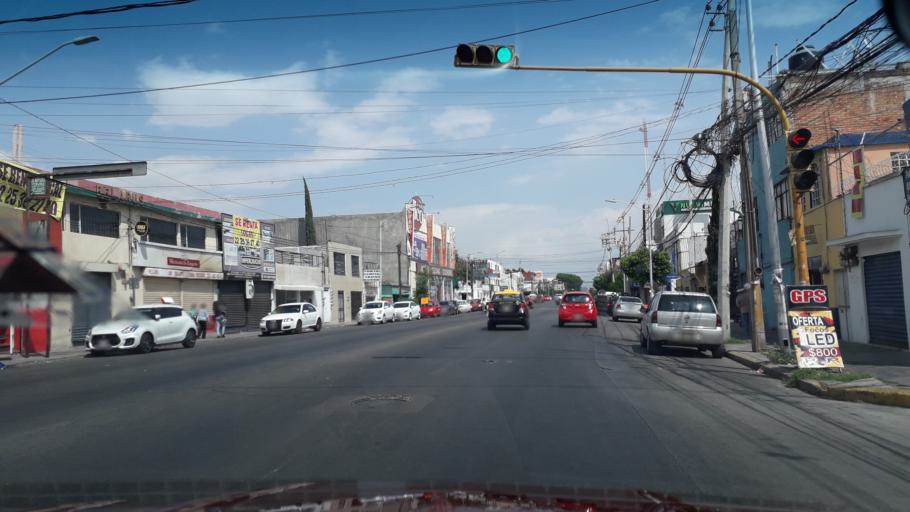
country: MX
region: Puebla
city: Puebla
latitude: 19.0404
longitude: -98.2203
